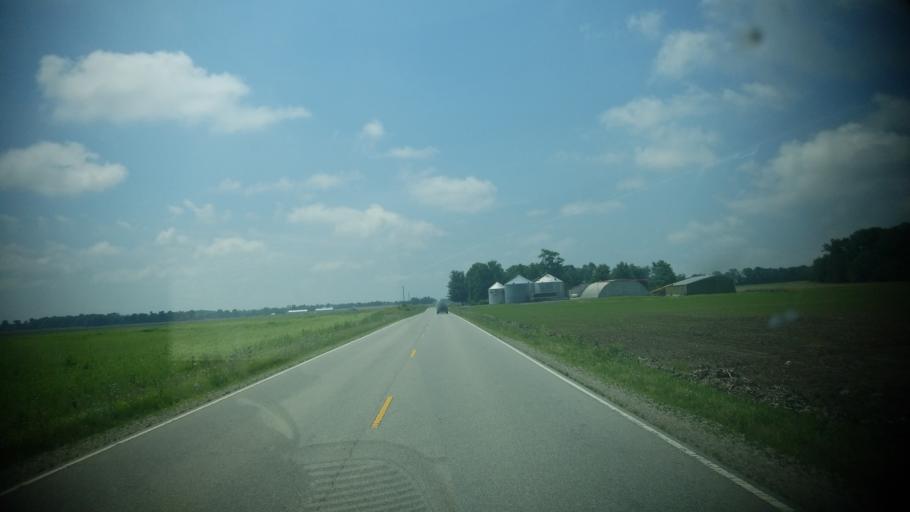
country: US
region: Illinois
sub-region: Wayne County
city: Fairfield
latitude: 38.4568
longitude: -88.3491
